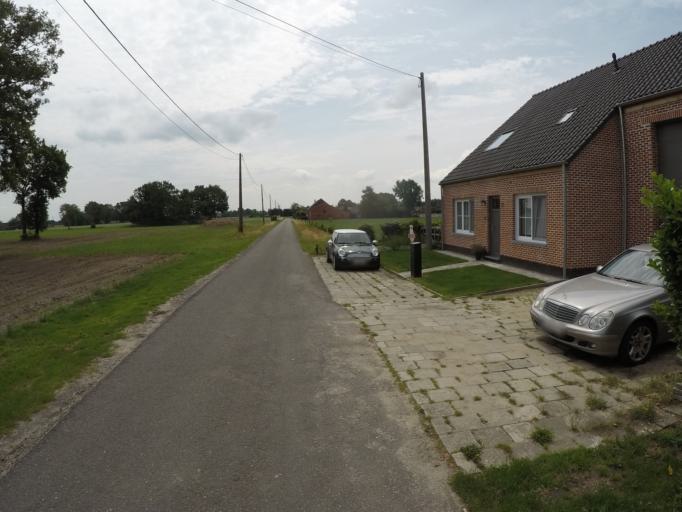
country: BE
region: Flanders
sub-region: Provincie Antwerpen
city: Essen
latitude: 51.4500
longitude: 4.5156
